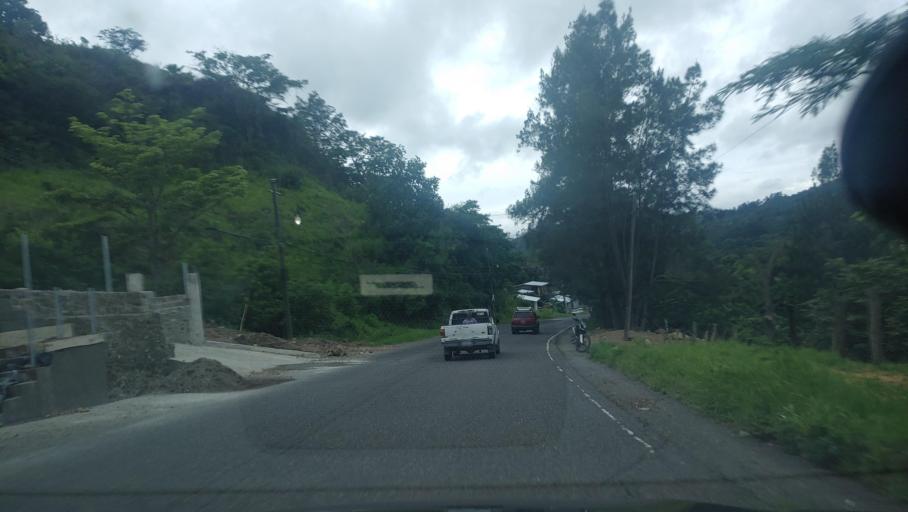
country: HN
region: Choluteca
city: San Marcos de Colon
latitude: 13.3764
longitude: -86.8904
